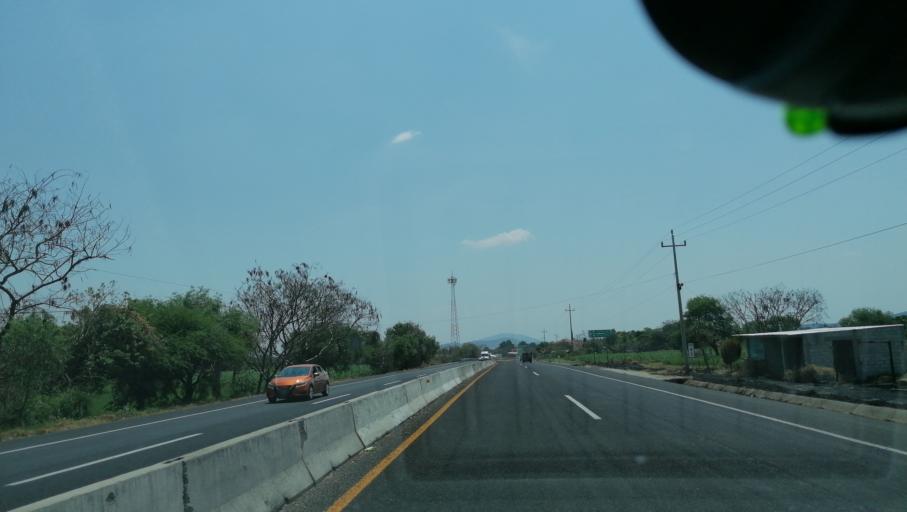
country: MX
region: Puebla
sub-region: Huaquechula
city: Tronconal
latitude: 18.7995
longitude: -98.4507
